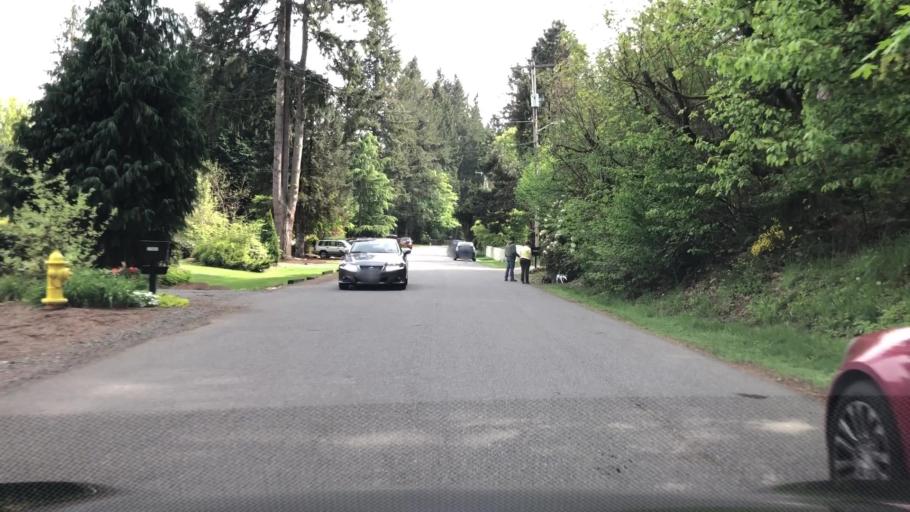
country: US
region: Washington
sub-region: King County
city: Cottage Lake
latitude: 47.7558
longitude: -122.0930
